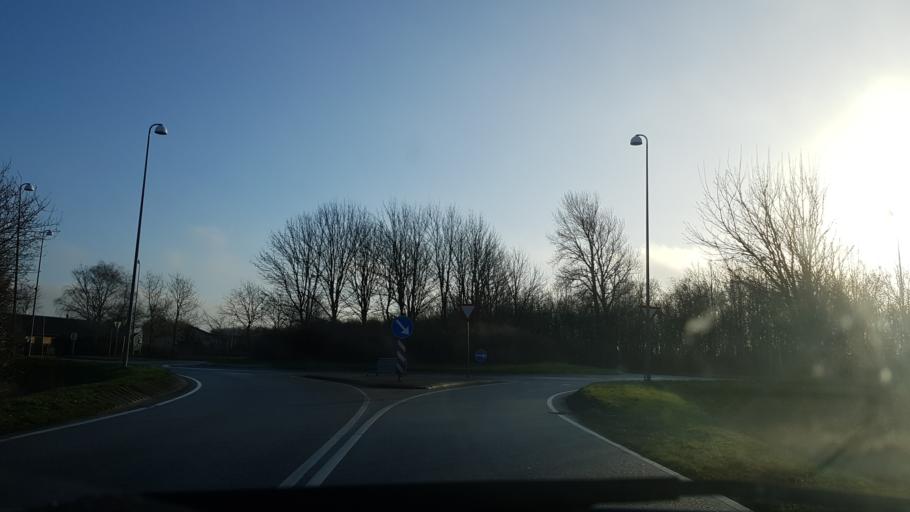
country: DK
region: South Denmark
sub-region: Haderslev Kommune
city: Vojens
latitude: 55.1992
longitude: 9.1965
